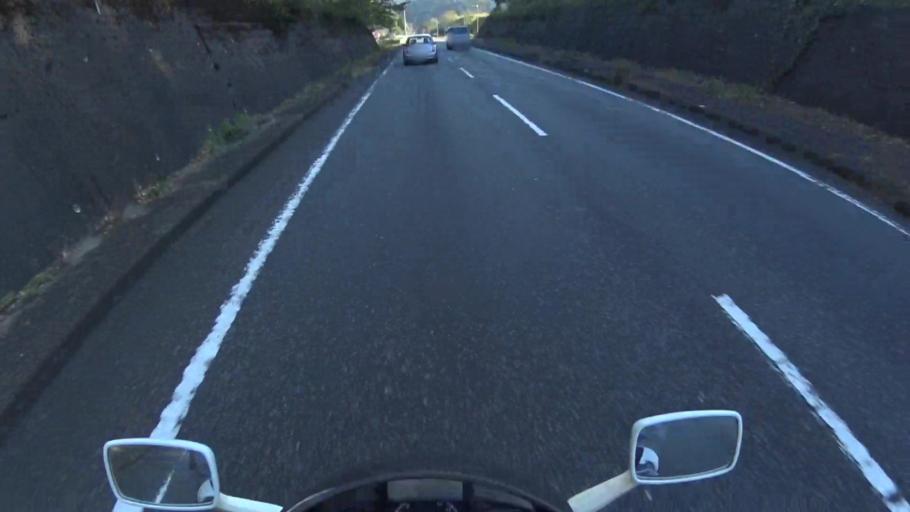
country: JP
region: Kyoto
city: Fukuchiyama
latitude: 35.3785
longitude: 135.0982
